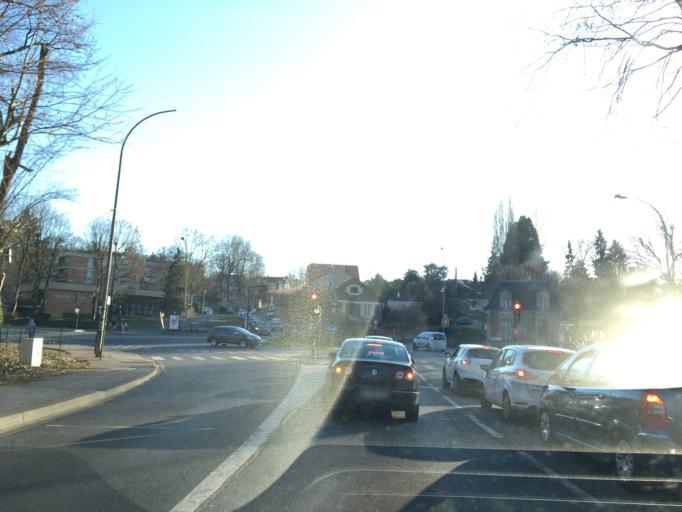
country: FR
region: Ile-de-France
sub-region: Departement de l'Essonne
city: Brunoy
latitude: 48.6954
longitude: 2.5027
